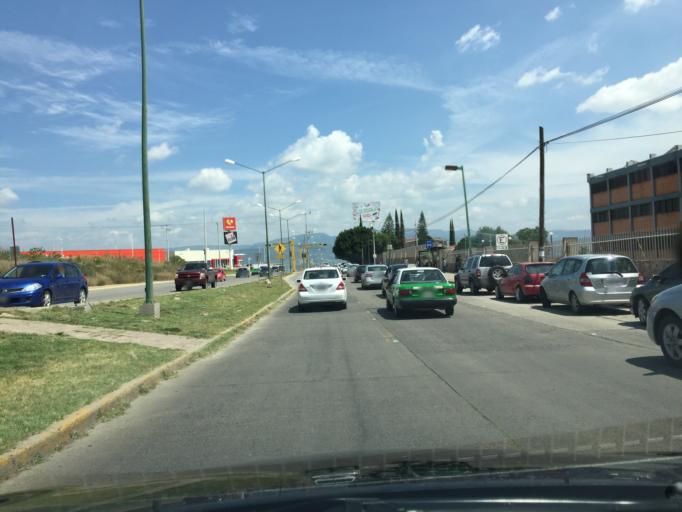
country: MX
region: Guanajuato
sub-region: Leon
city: La Ermita
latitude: 21.1542
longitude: -101.7114
